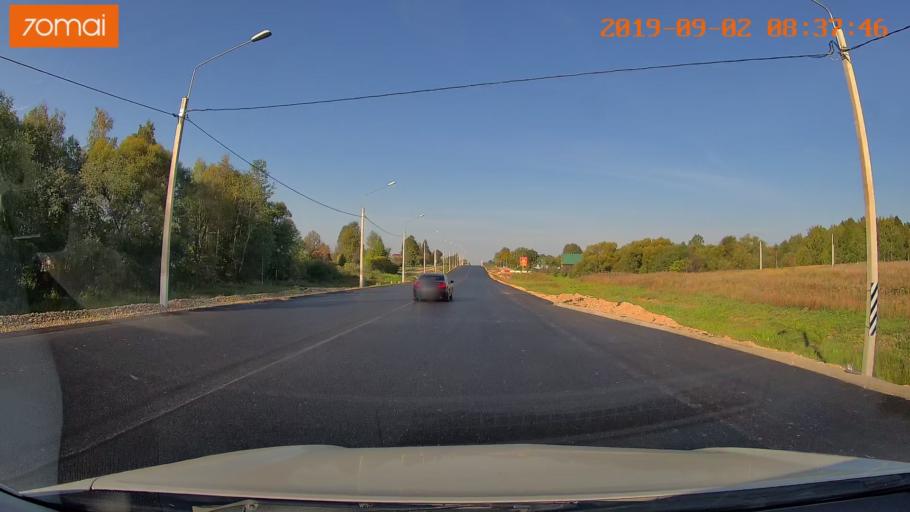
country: RU
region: Kaluga
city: Kudinovo
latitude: 54.9789
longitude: 36.1922
